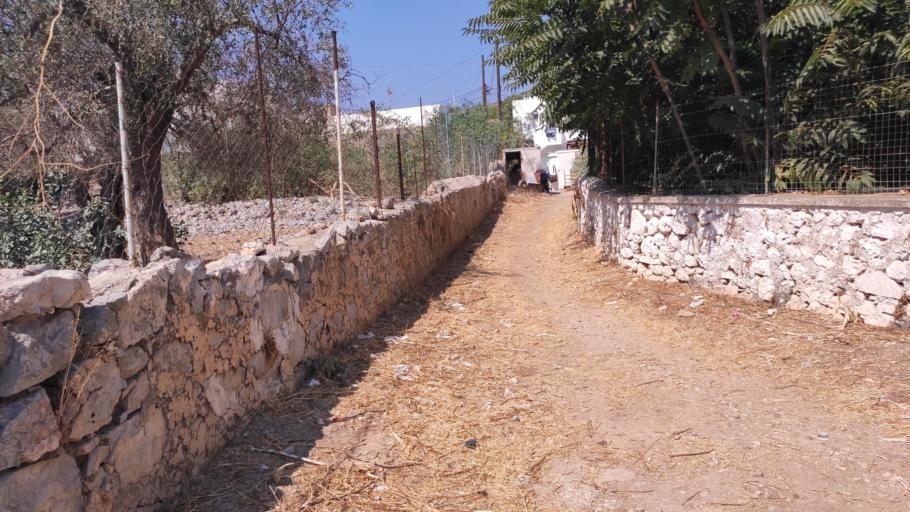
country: GR
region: South Aegean
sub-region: Nomos Dodekanisou
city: Pylion
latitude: 36.9327
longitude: 27.1353
